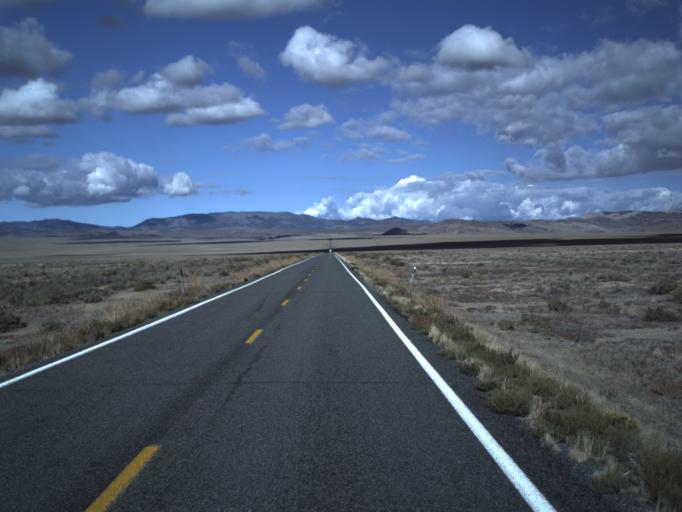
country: US
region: Utah
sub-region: Beaver County
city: Milford
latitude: 38.5407
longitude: -113.7043
